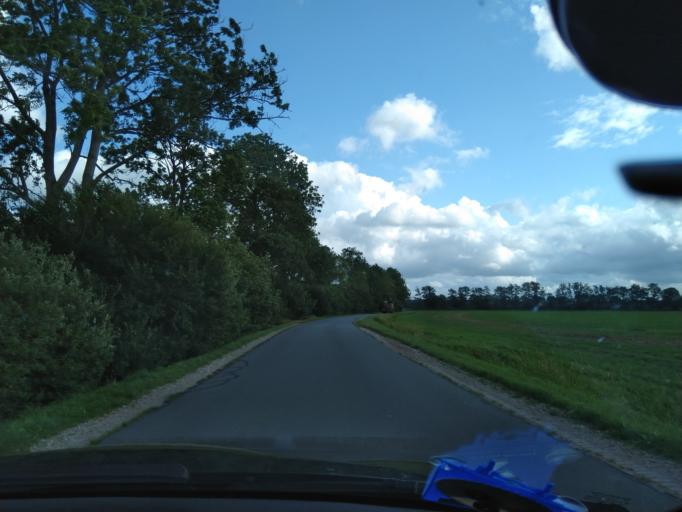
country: NL
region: Drenthe
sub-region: Gemeente Tynaarlo
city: Vries
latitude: 53.0898
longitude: 6.5350
